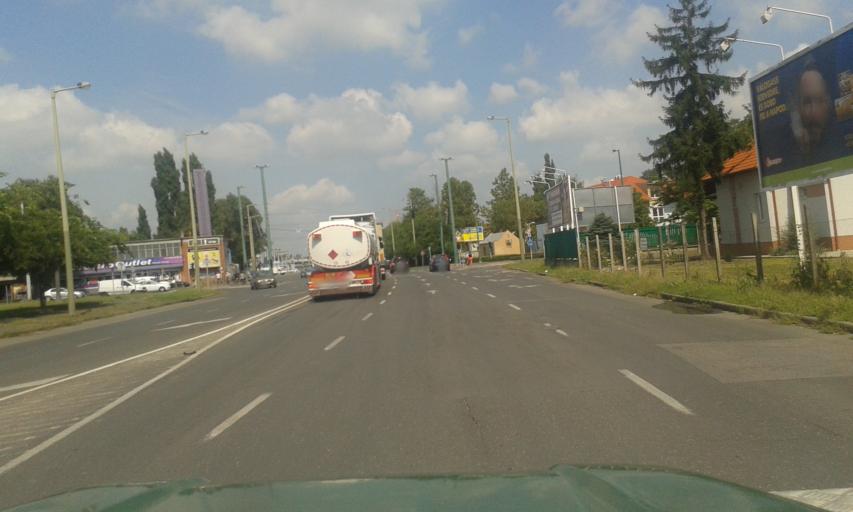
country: HU
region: Csongrad
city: Szeged
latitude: 46.2525
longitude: 20.1234
